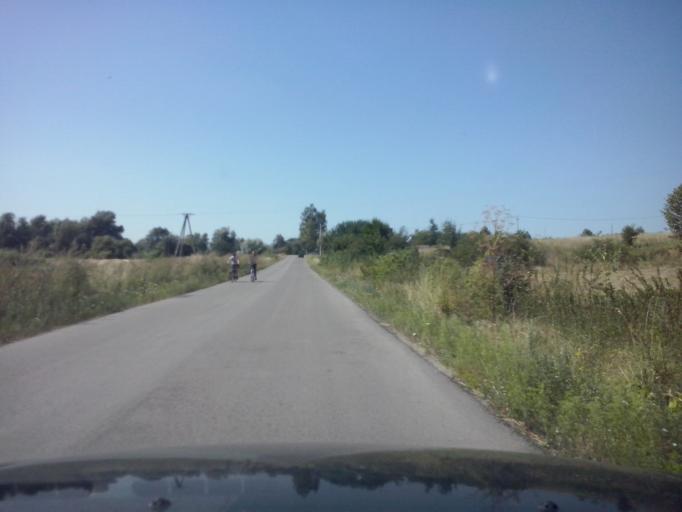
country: PL
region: Swietokrzyskie
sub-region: Powiat kielecki
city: Chmielnik
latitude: 50.6108
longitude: 20.7682
